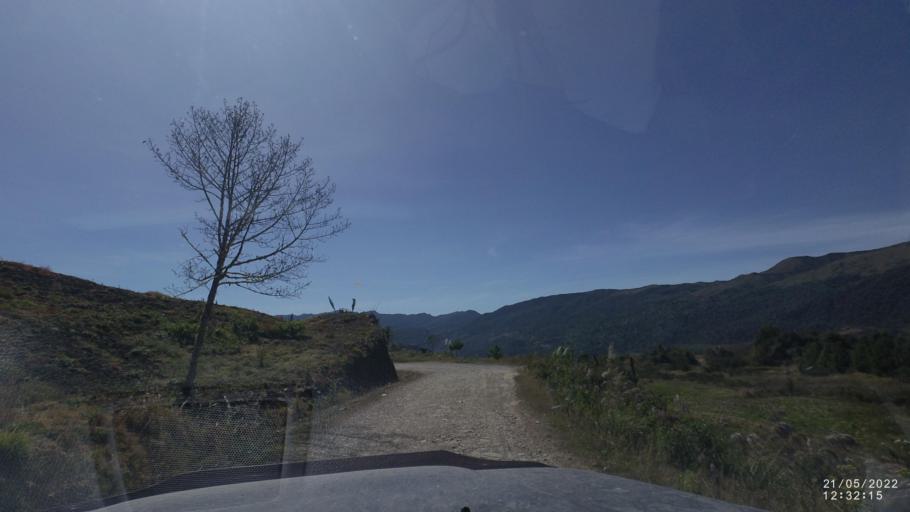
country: BO
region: Cochabamba
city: Colomi
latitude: -17.2071
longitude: -65.9149
